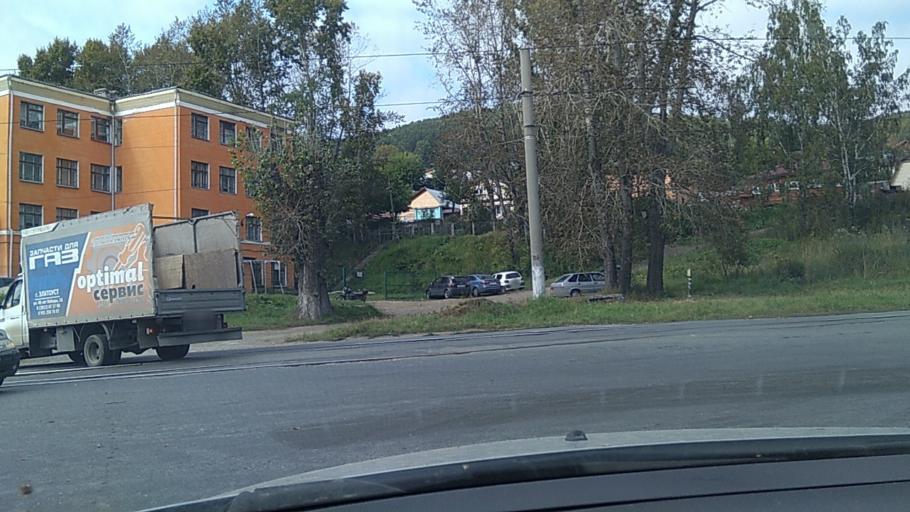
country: RU
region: Chelyabinsk
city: Zlatoust
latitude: 55.1782
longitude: 59.7011
